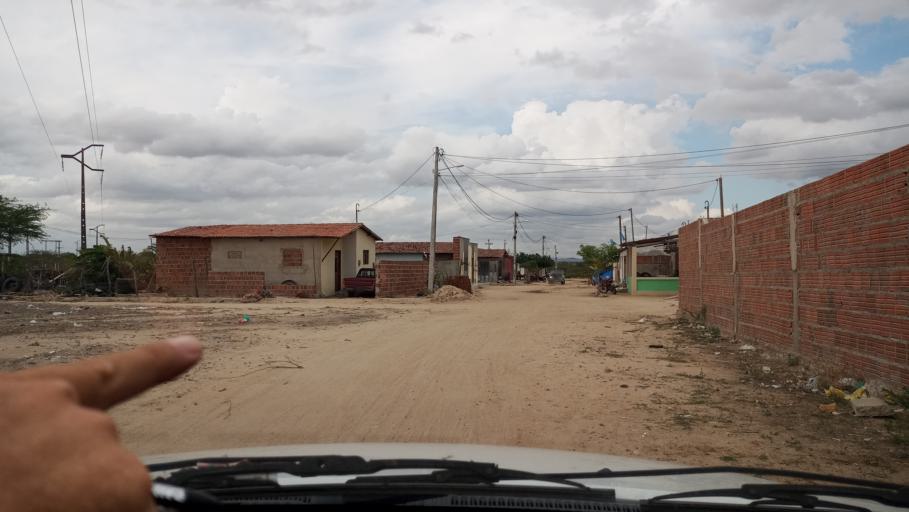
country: BR
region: Rio Grande do Norte
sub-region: Tangara
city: Tangara
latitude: -6.1910
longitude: -35.8028
